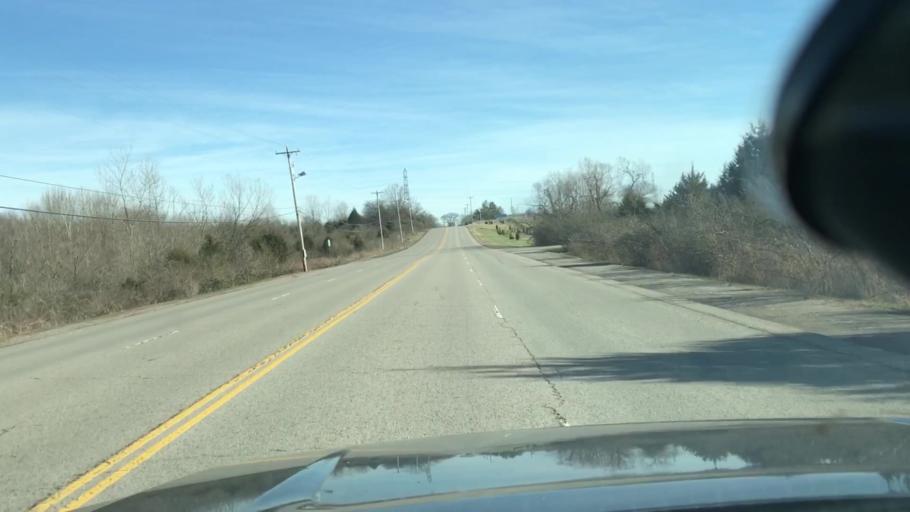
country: US
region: Tennessee
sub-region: Davidson County
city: Nashville
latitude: 36.1858
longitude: -86.8578
